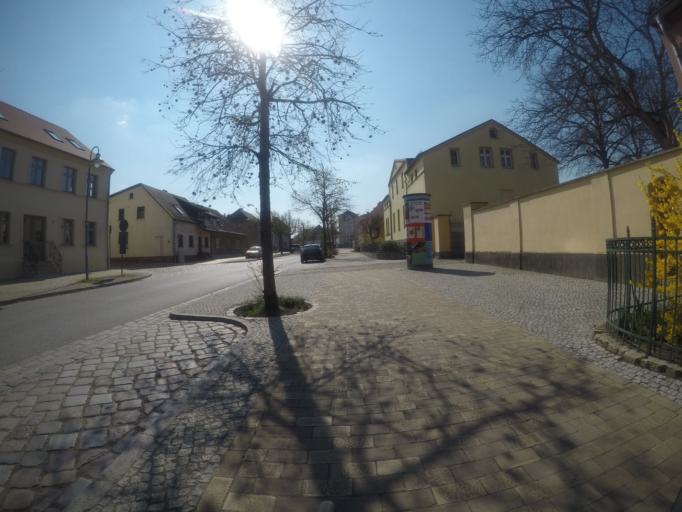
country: DE
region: Brandenburg
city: Ketzin
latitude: 52.4781
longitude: 12.8422
